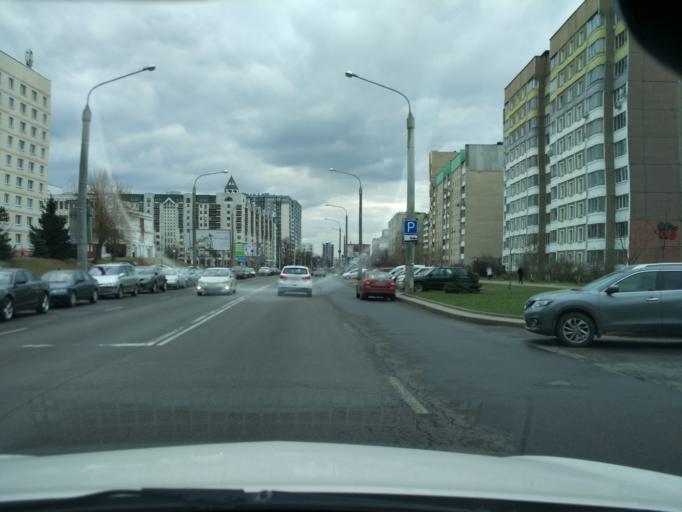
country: BY
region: Minsk
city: Minsk
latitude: 53.9350
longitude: 27.5918
